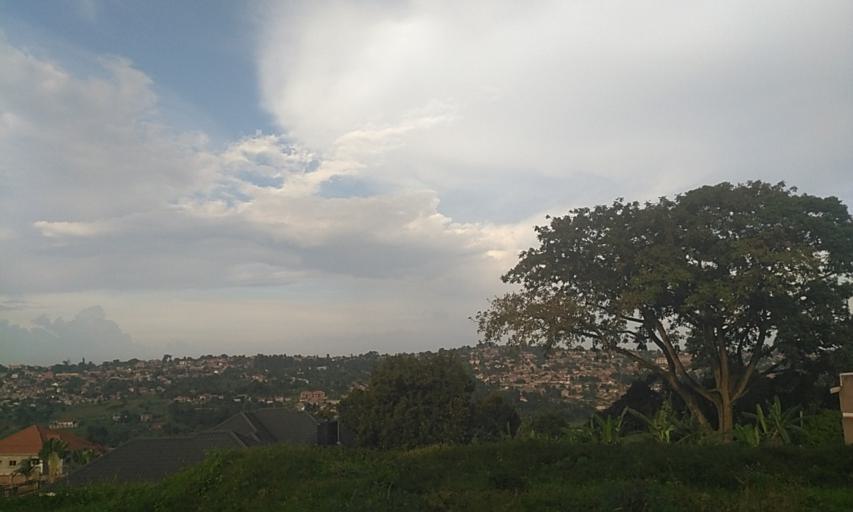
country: UG
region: Central Region
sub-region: Wakiso District
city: Kajansi
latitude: 0.2601
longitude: 32.5301
